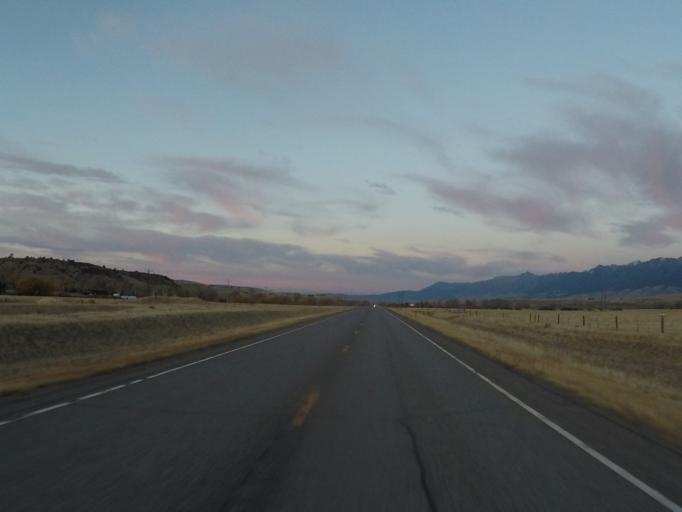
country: US
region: Montana
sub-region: Park County
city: Livingston
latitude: 45.3520
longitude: -110.7498
